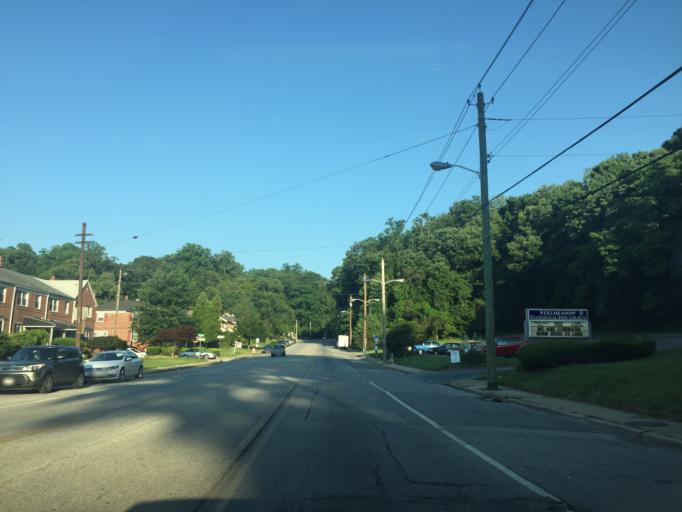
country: US
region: Maryland
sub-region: Baltimore County
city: Charlestown
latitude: 39.2813
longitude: -76.6995
